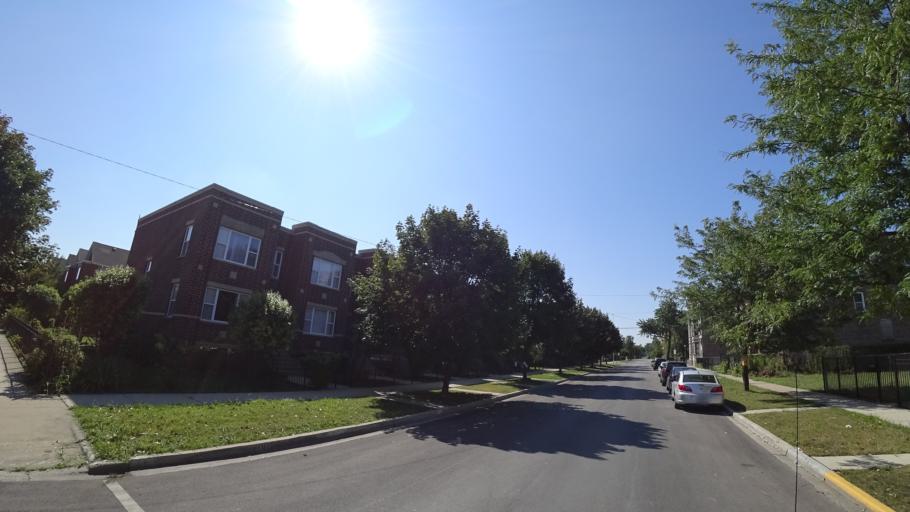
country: US
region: Illinois
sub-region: Cook County
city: Cicero
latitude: 41.8651
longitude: -87.7130
